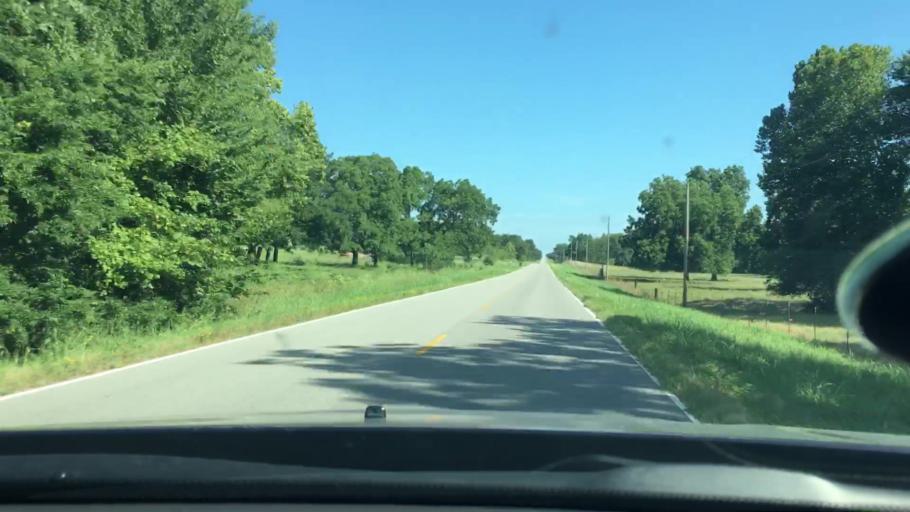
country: US
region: Oklahoma
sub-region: Johnston County
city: Tishomingo
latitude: 34.2835
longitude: -96.5487
